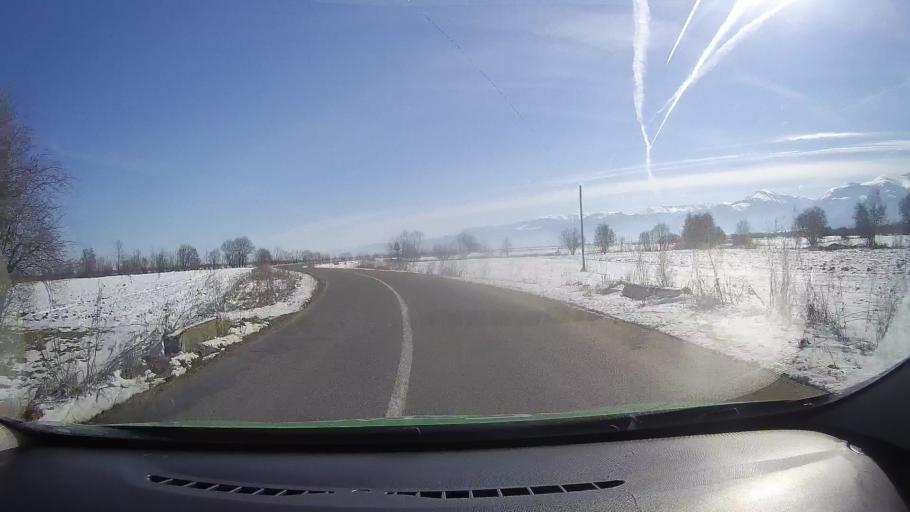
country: RO
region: Brasov
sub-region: Comuna Sambata de Sus
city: Sambata de Sus
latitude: 45.7475
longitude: 24.8397
